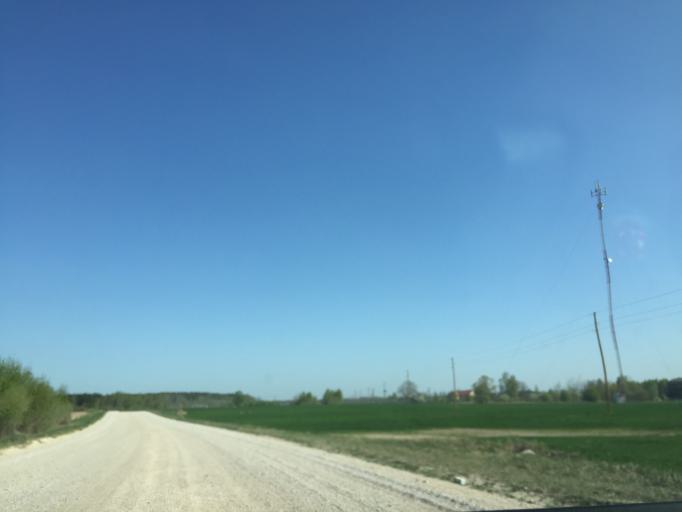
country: LV
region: Malpils
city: Malpils
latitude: 56.8926
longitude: 24.9353
